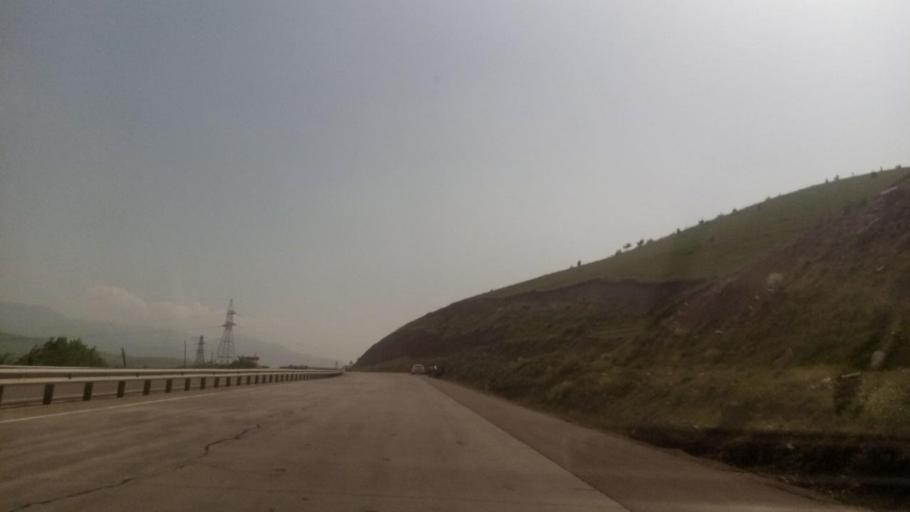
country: UZ
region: Toshkent
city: Angren
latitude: 41.0714
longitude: 70.2331
